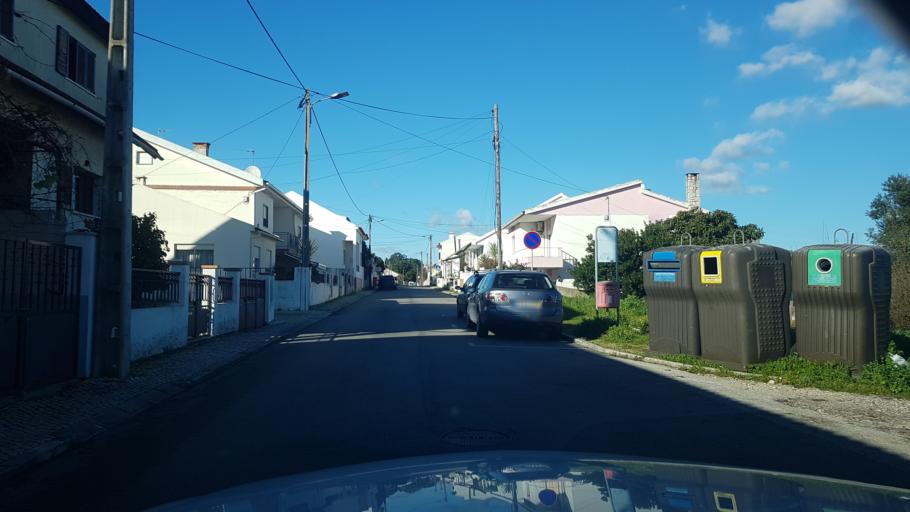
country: PT
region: Santarem
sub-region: Entroncamento
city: Entroncamento
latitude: 39.4744
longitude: -8.4796
